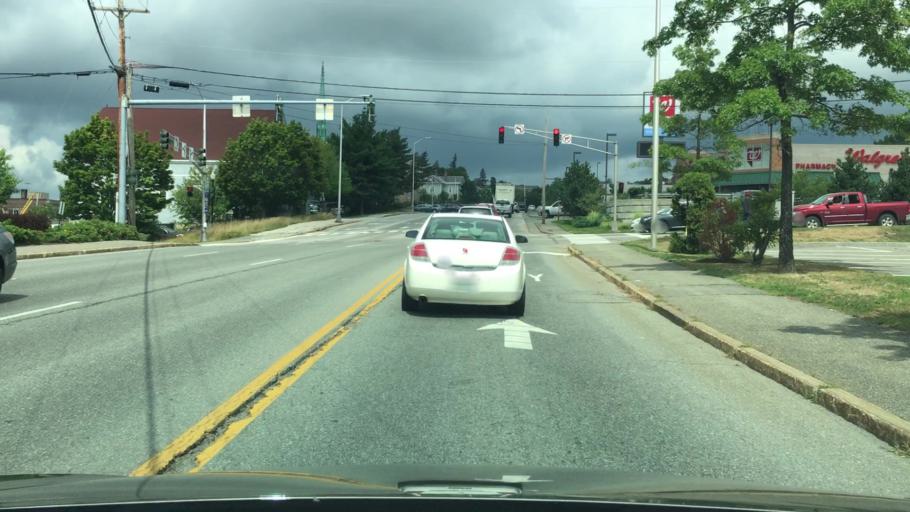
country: US
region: Maine
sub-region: Penobscot County
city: Brewer
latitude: 44.8007
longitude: -68.7664
